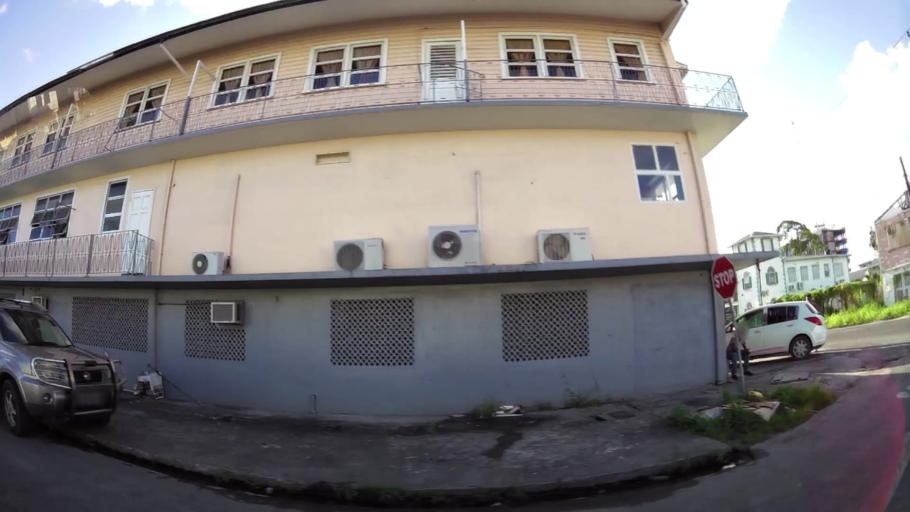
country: GY
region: Demerara-Mahaica
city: Georgetown
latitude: 6.8149
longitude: -58.1578
